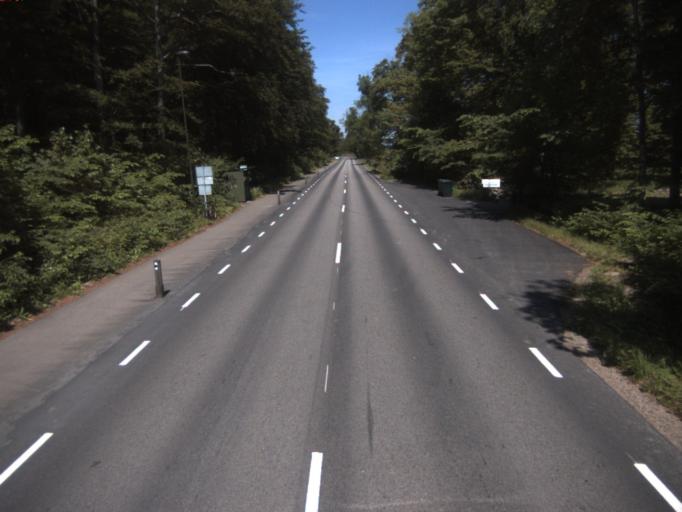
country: DK
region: Capital Region
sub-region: Helsingor Kommune
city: Helsingor
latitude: 56.1079
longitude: 12.6385
